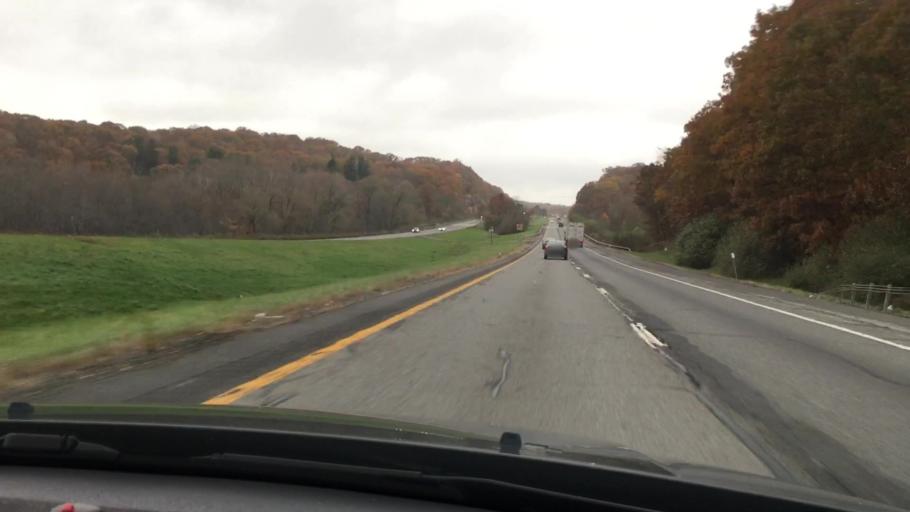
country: US
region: New York
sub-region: Putnam County
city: Lake Carmel
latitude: 41.4484
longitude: -73.6362
